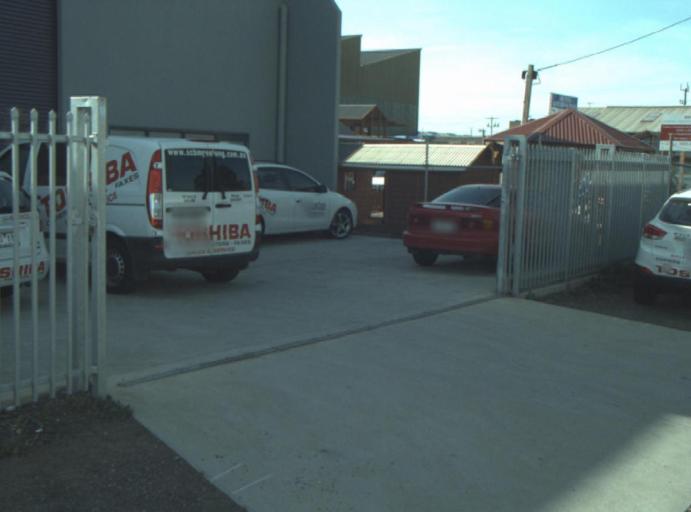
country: AU
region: Victoria
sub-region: Greater Geelong
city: Bell Park
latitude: -38.1131
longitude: 144.3495
